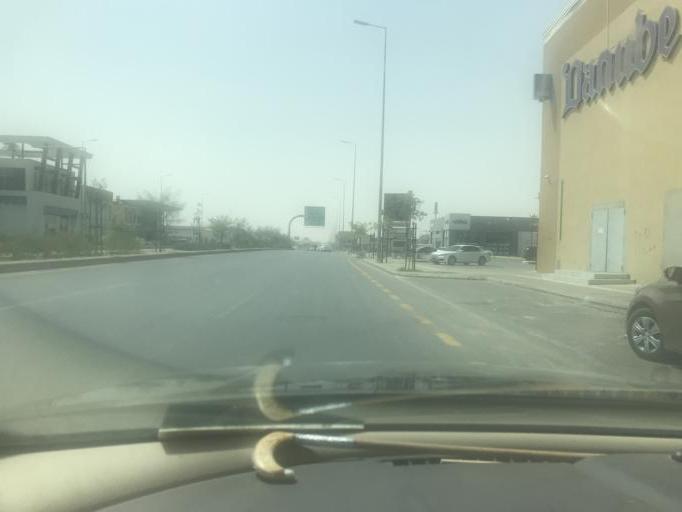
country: SA
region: Ar Riyad
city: Riyadh
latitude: 24.7347
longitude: 46.7839
